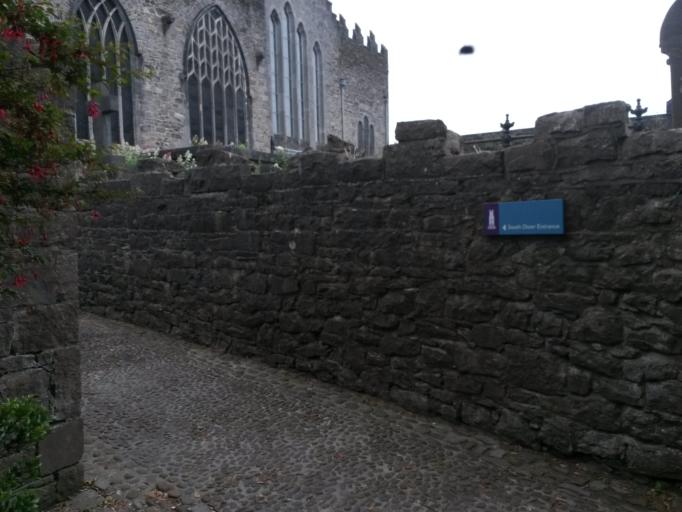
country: IE
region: Munster
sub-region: County Limerick
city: Luimneach
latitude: 52.6679
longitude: -8.6234
